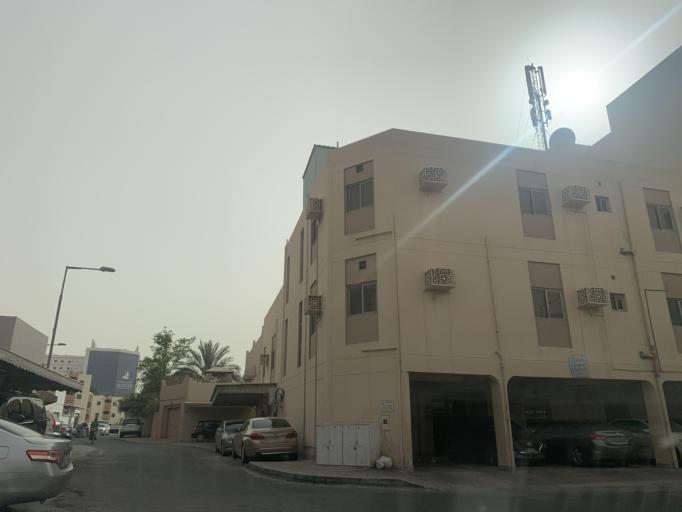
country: BH
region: Northern
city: Madinat `Isa
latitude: 26.1568
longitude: 50.5711
